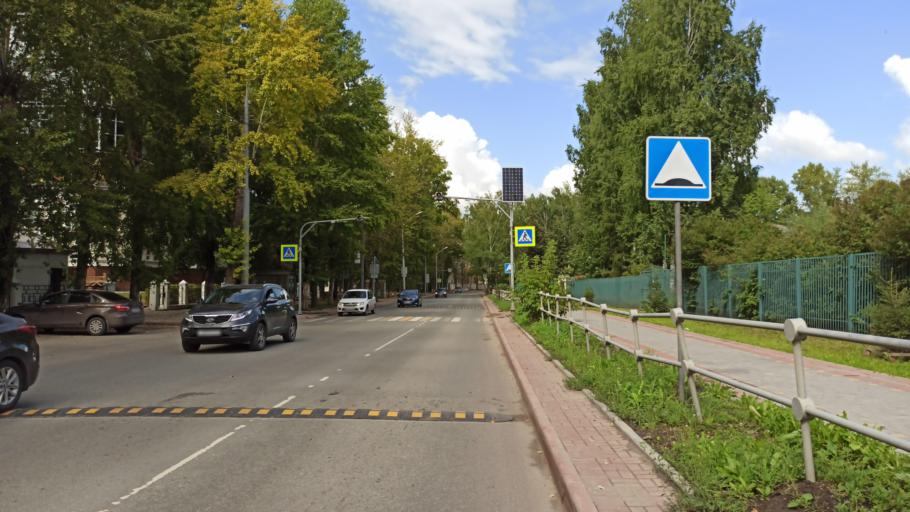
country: RU
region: Tomsk
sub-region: Tomskiy Rayon
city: Tomsk
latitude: 56.4615
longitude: 84.9816
